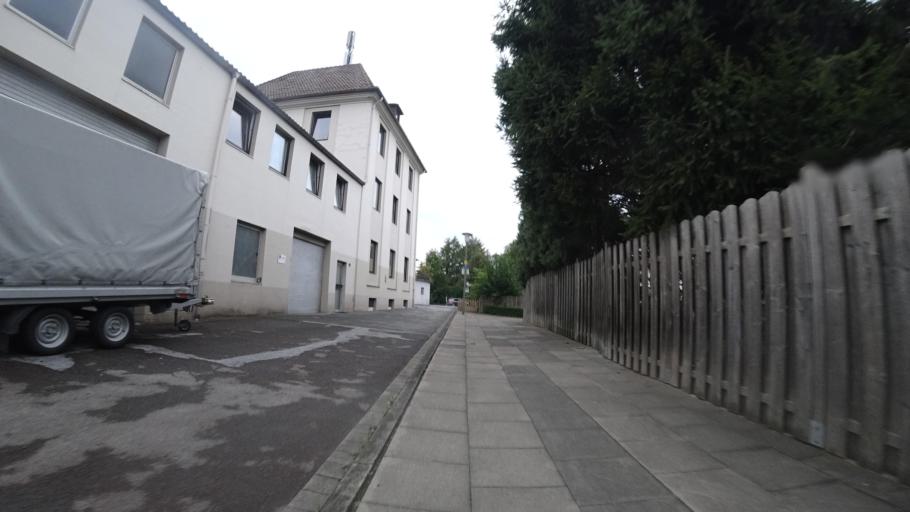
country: DE
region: North Rhine-Westphalia
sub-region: Regierungsbezirk Detmold
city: Bielefeld
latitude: 52.0516
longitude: 8.5524
